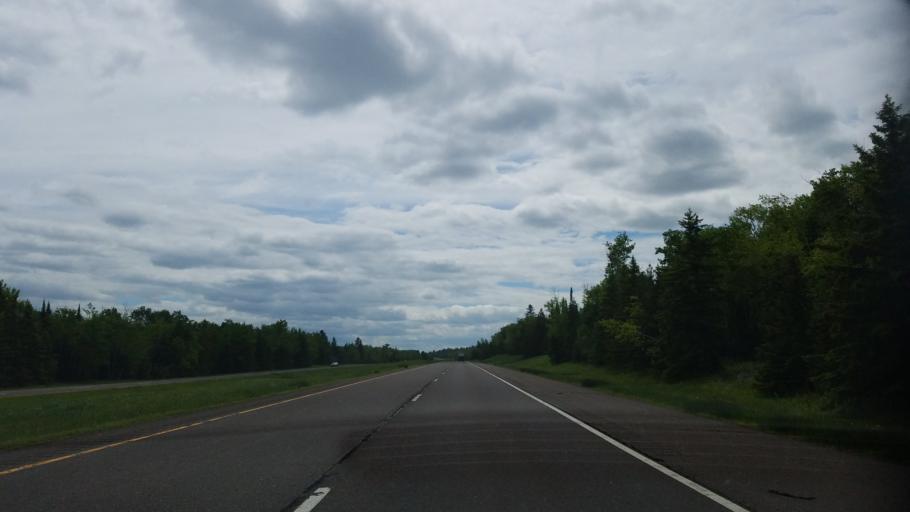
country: US
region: Minnesota
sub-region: Lake County
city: Two Harbors
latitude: 47.0058
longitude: -91.7174
